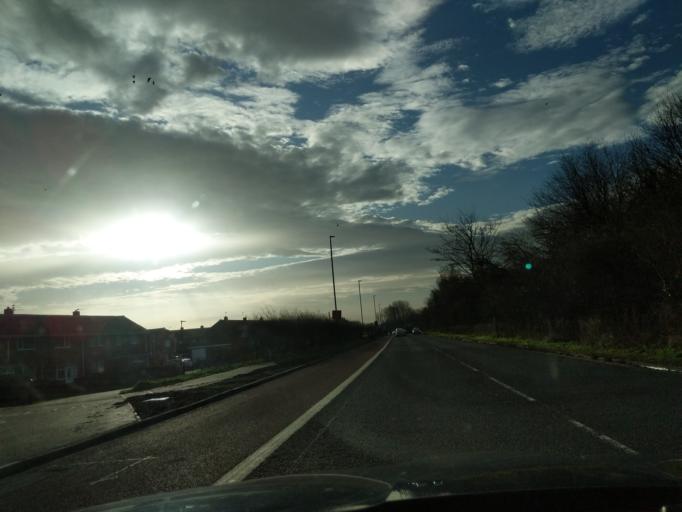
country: GB
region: England
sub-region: Newcastle upon Tyne
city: Gosforth
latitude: 55.0158
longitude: -1.5996
